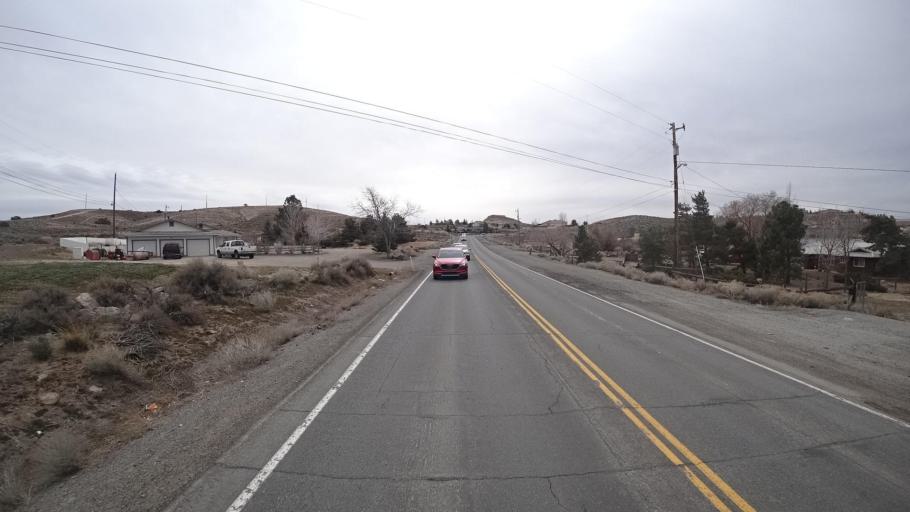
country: US
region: Nevada
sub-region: Washoe County
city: Golden Valley
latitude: 39.6073
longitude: -119.8127
